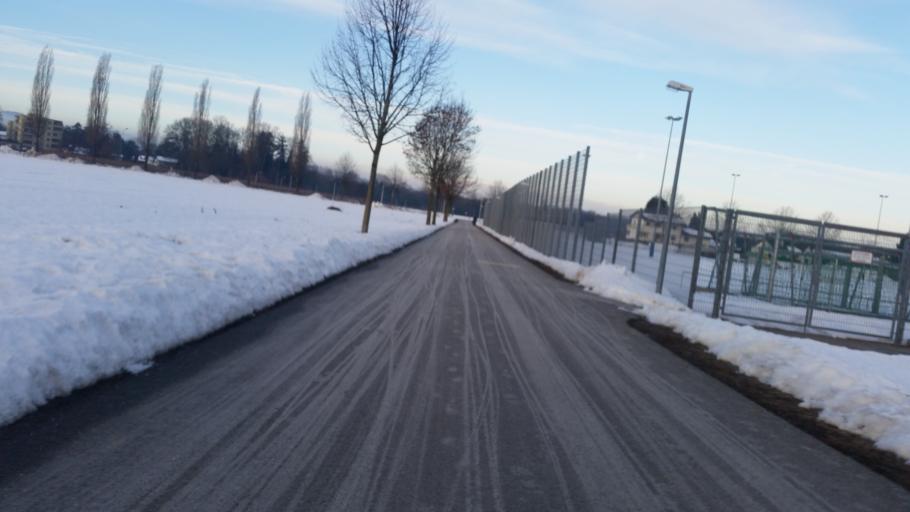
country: AT
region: Vorarlberg
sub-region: Politischer Bezirk Bregenz
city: Lauterach
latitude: 47.5017
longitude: 9.7126
